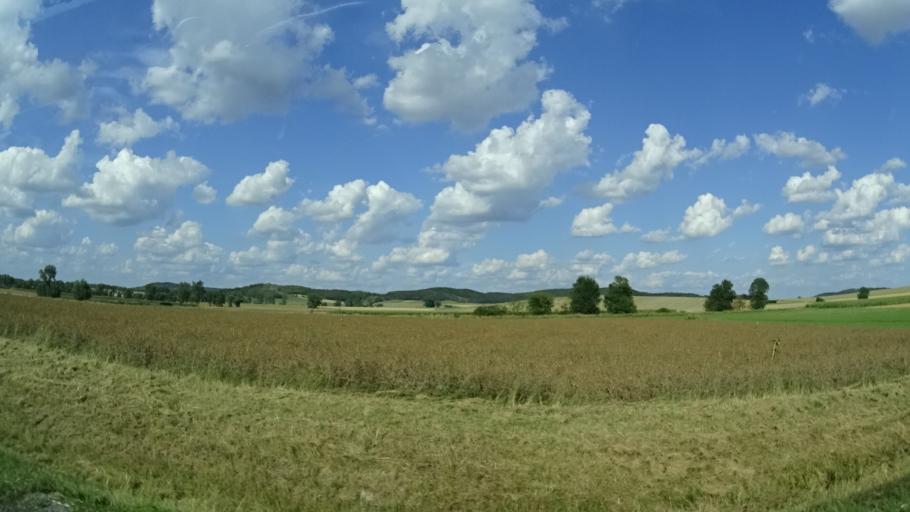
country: DE
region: Bavaria
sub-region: Regierungsbezirk Unterfranken
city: Bad Konigshofen im Grabfeld
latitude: 50.2826
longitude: 10.4908
